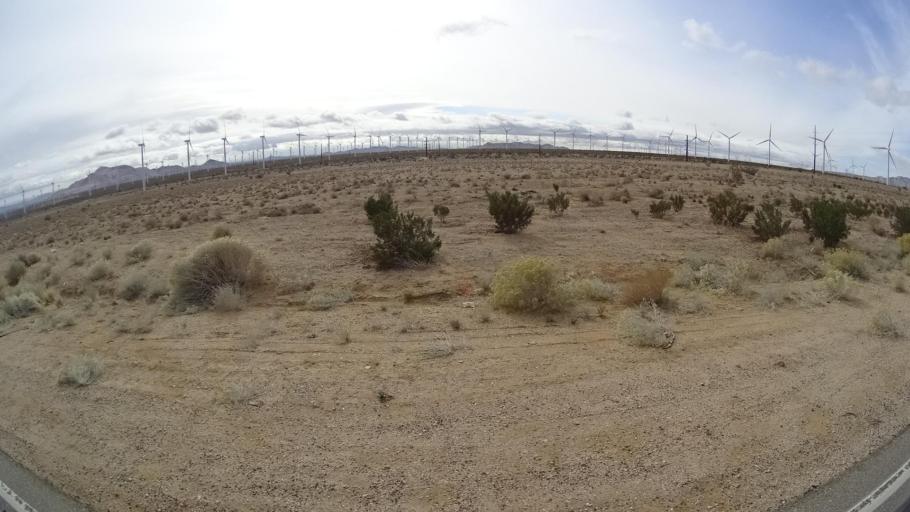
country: US
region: California
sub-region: Kern County
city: Mojave
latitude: 35.0385
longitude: -118.2627
